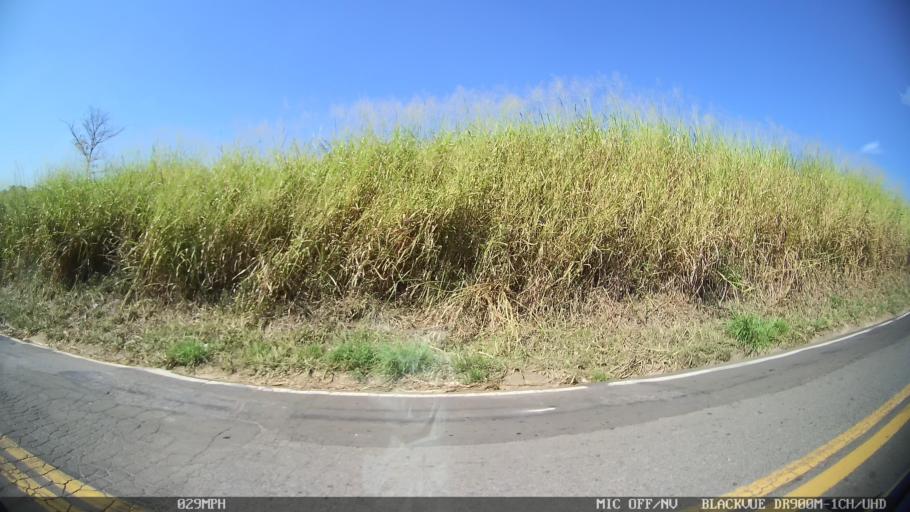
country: BR
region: Sao Paulo
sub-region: Valinhos
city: Valinhos
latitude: -23.0139
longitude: -47.0939
